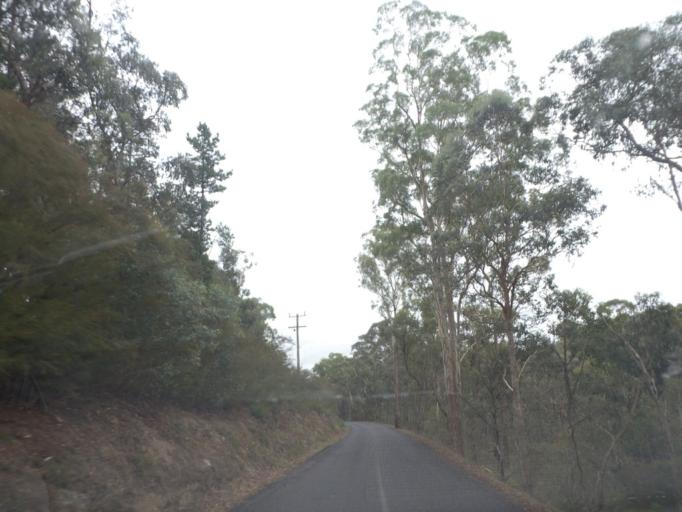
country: AU
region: Victoria
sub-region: Nillumbik
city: Saint Andrews
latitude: -37.5987
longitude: 145.2860
